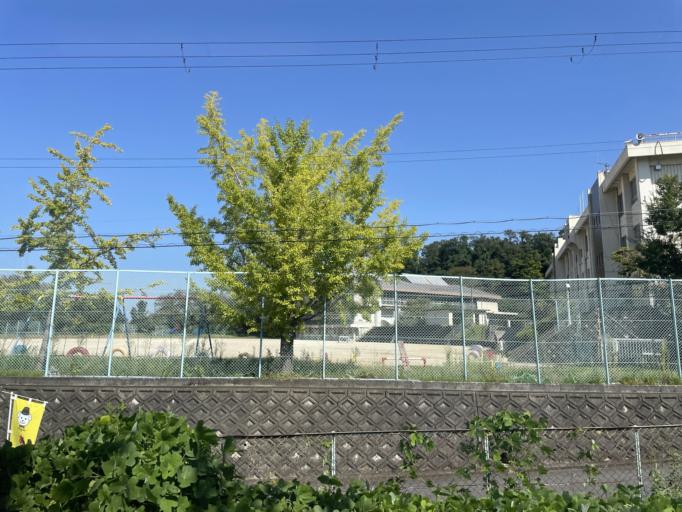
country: JP
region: Nara
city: Tawaramoto
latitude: 34.5916
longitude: 135.7117
